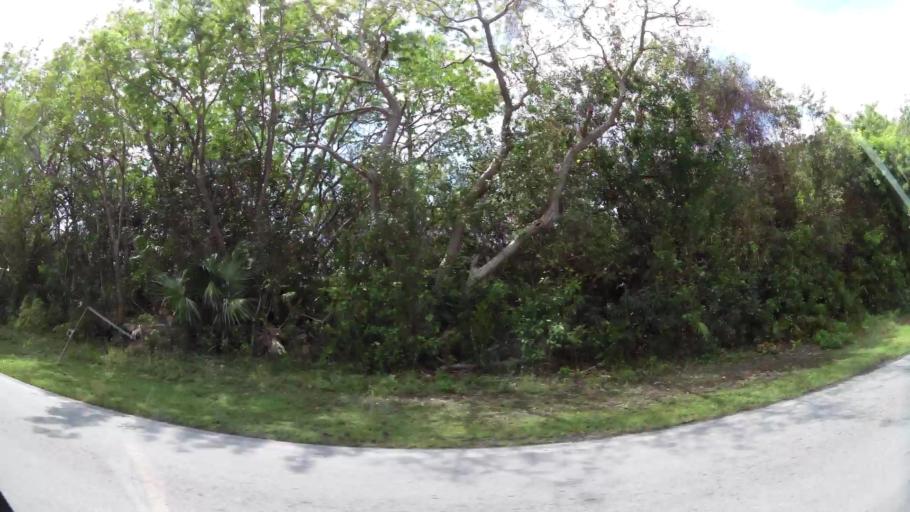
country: BS
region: Freeport
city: Lucaya
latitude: 26.5309
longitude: -78.6569
